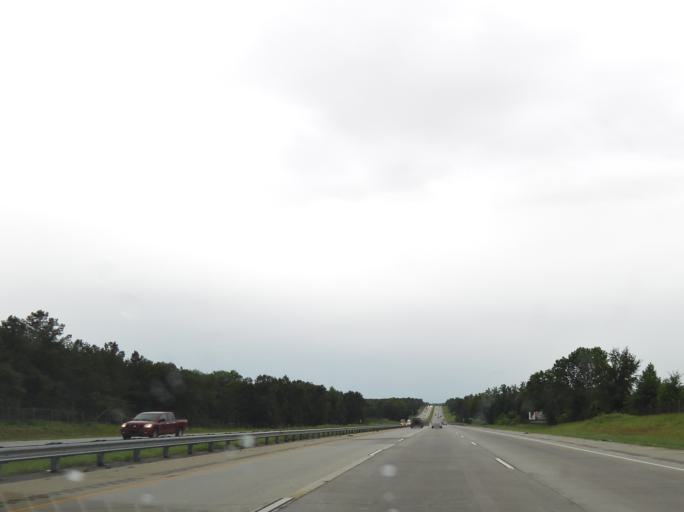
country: US
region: Georgia
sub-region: Dooly County
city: Unadilla
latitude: 32.3263
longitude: -83.7658
